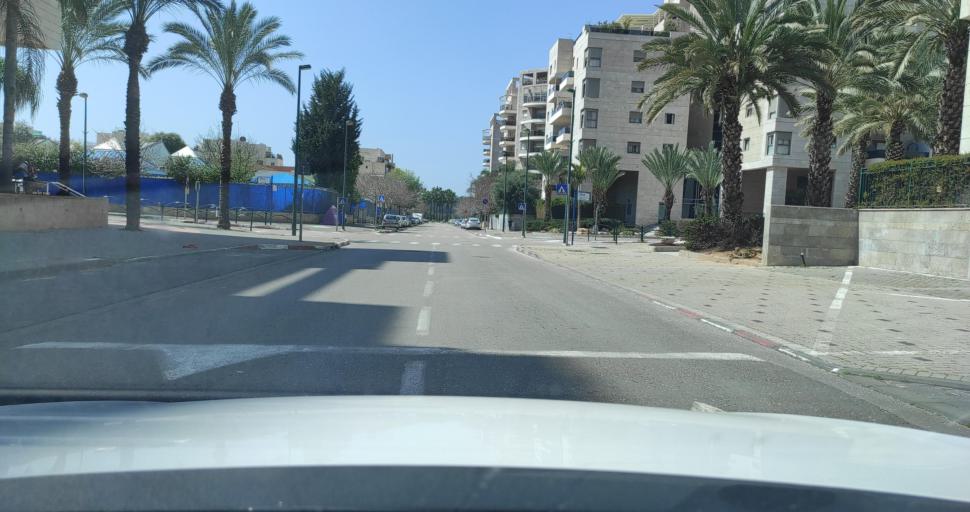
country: IL
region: Central District
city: Nordiyya
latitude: 32.3003
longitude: 34.8720
